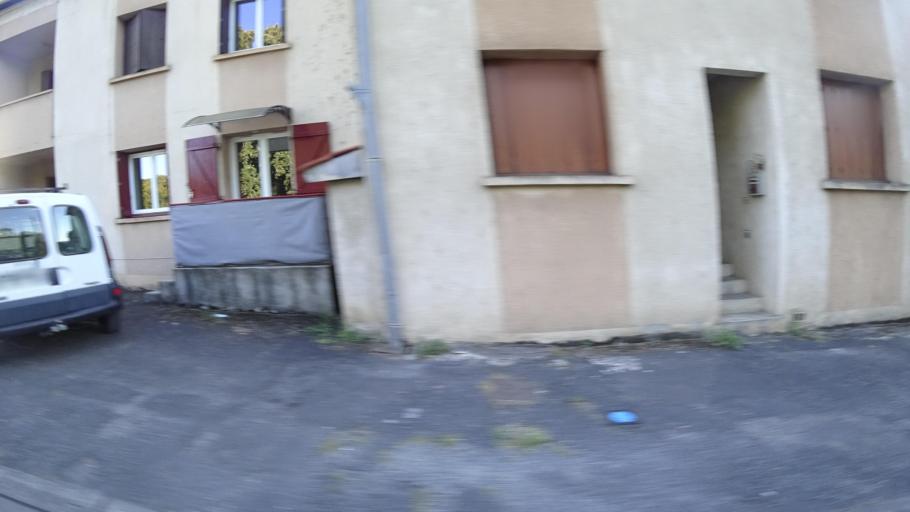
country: FR
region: Midi-Pyrenees
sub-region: Departement de l'Aveyron
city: Cransac
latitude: 44.5240
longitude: 2.2884
